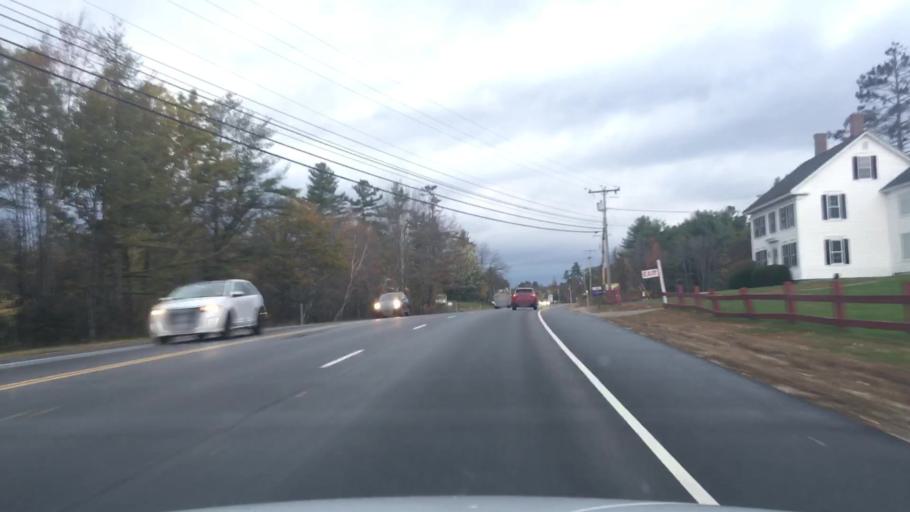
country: US
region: New Hampshire
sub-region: Merrimack County
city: Chichester
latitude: 43.2388
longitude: -71.3937
